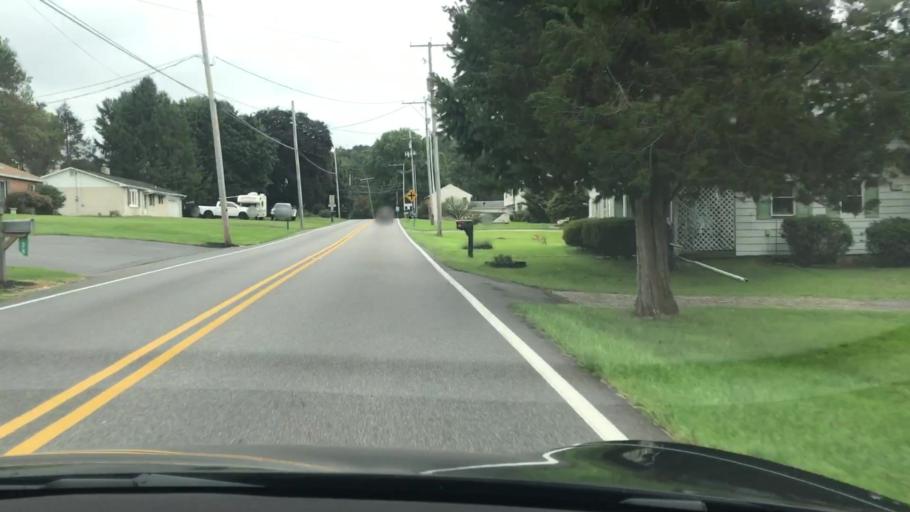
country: US
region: Pennsylvania
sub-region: York County
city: Dillsburg
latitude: 40.1040
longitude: -77.0581
